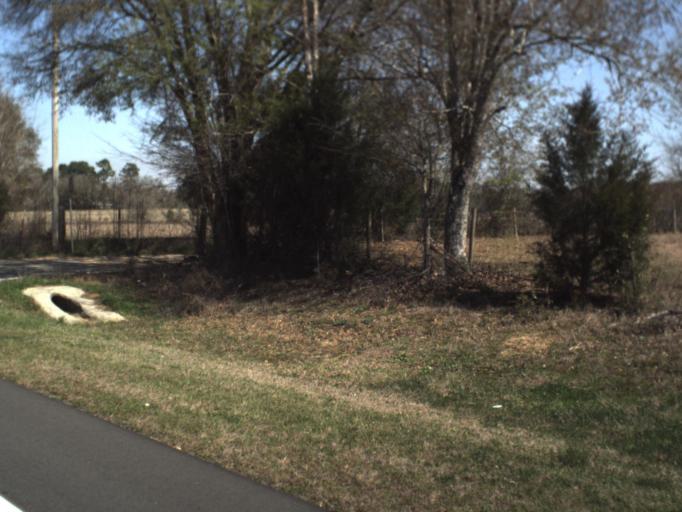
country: US
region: Florida
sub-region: Jackson County
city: Sneads
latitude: 30.7701
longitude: -85.0191
